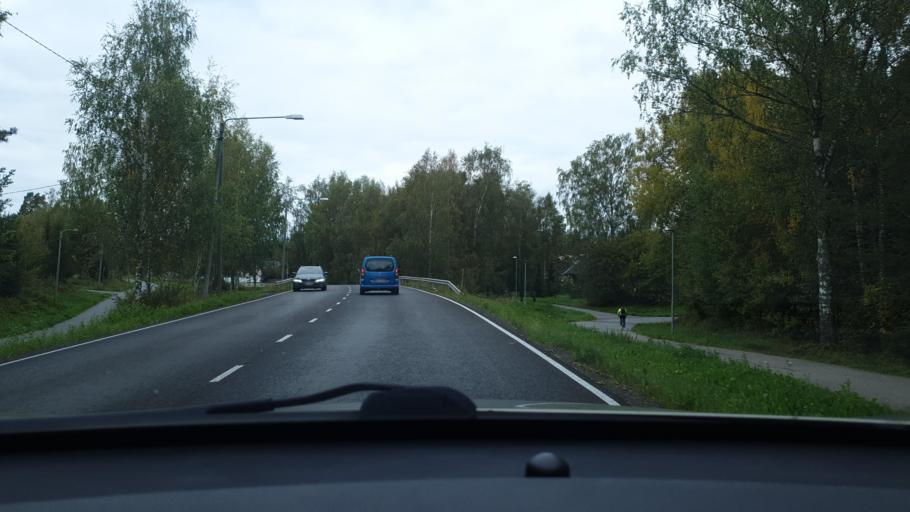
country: FI
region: Ostrobothnia
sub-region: Vaasa
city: Teeriniemi
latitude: 63.0889
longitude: 21.6908
